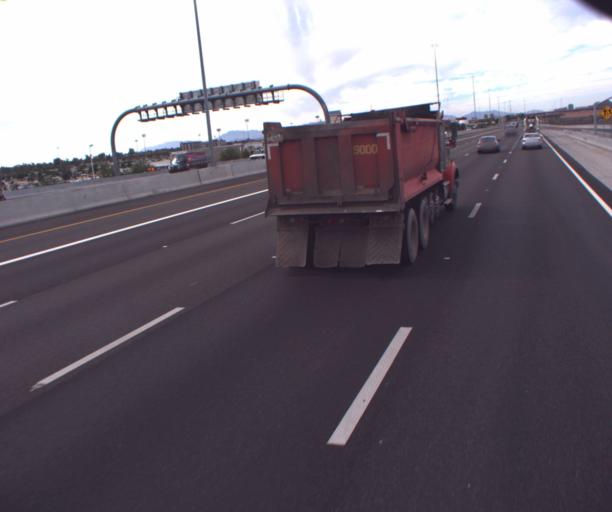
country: US
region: Arizona
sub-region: Maricopa County
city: Tempe
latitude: 33.4373
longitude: -111.8712
